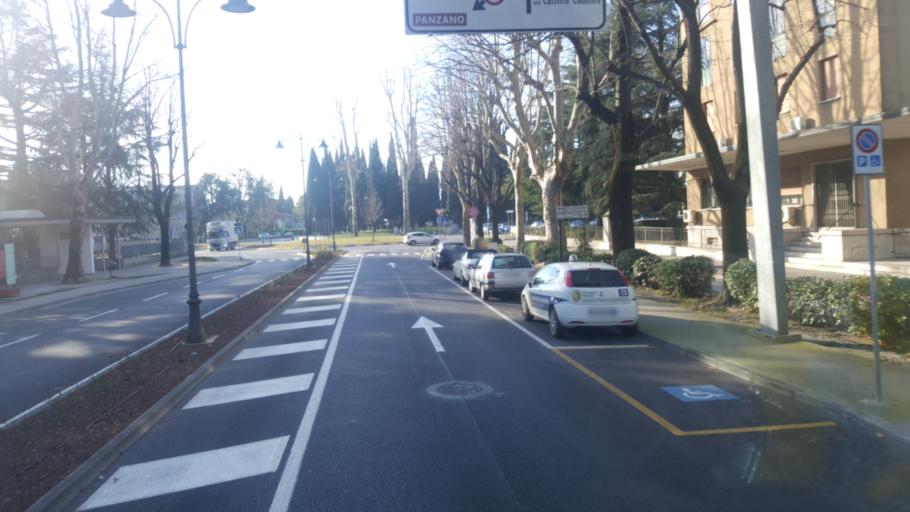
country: IT
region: Friuli Venezia Giulia
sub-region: Provincia di Gorizia
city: Monfalcone
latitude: 45.8021
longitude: 13.5310
